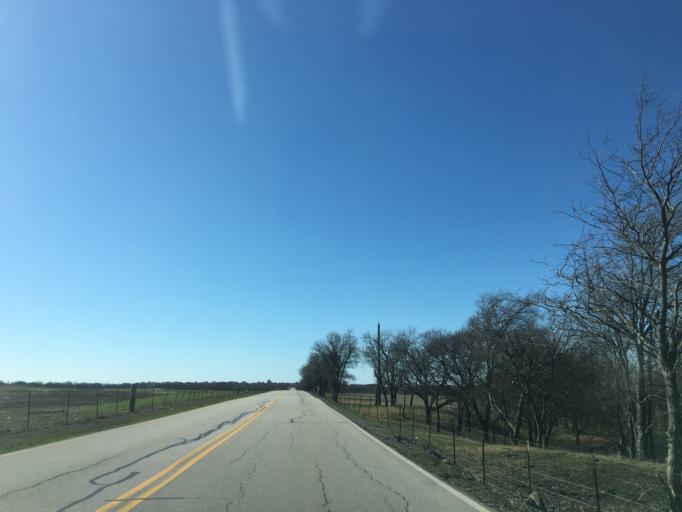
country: US
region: Texas
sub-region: Collin County
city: Prosper
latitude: 33.2336
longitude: -96.8336
